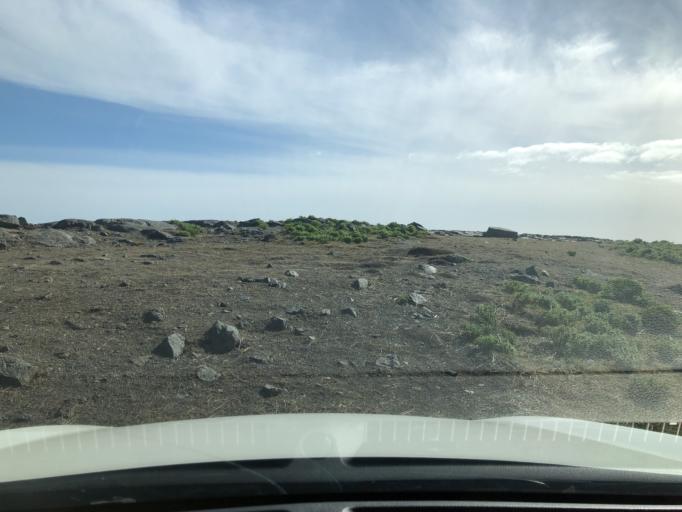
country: IS
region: East
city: Hoefn
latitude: 64.2402
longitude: -14.9710
